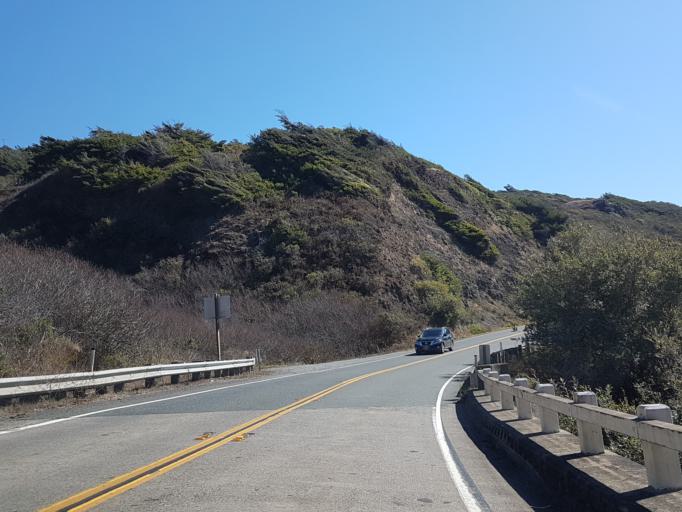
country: US
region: California
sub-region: Sonoma County
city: Monte Rio
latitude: 38.4707
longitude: -123.1537
